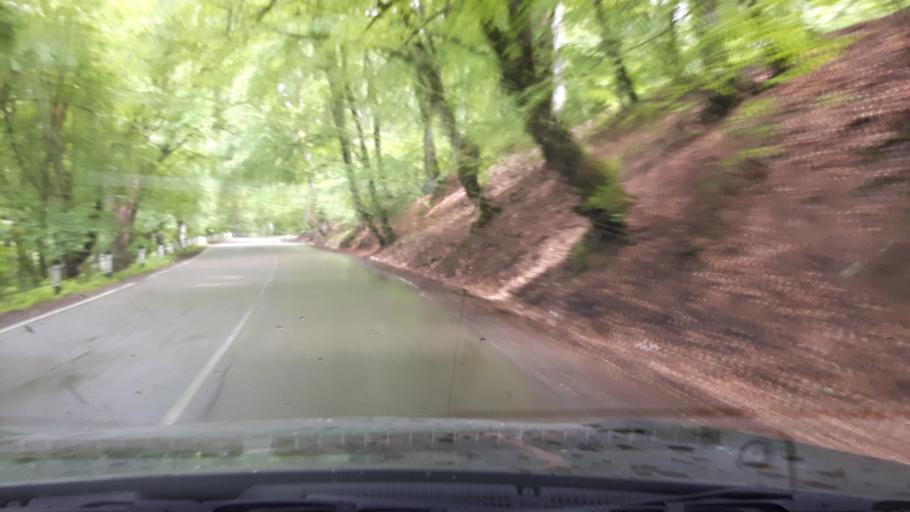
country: GE
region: Kakheti
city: Sagarejo
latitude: 41.8640
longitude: 45.3330
